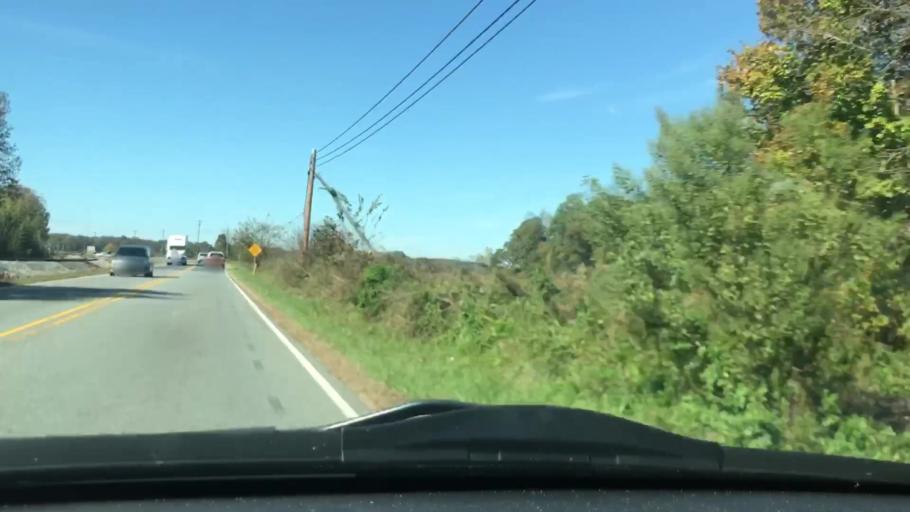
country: US
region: North Carolina
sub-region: Randolph County
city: Randleman
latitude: 35.8185
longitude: -79.8469
